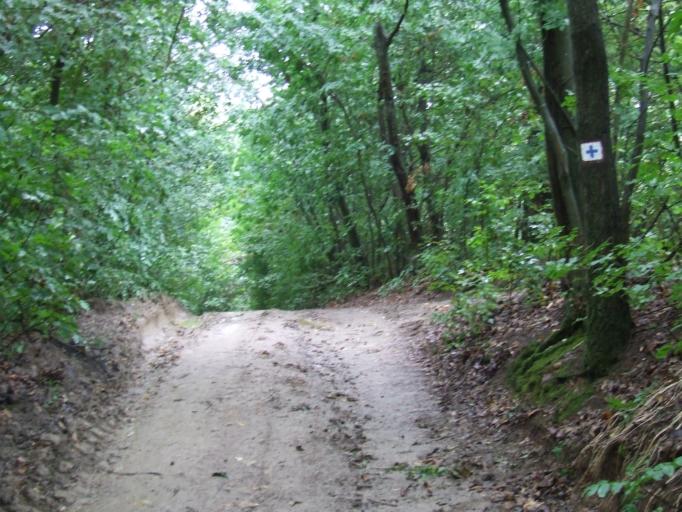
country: HU
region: Somogy
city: Kaposvar
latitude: 46.2959
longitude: 17.8072
